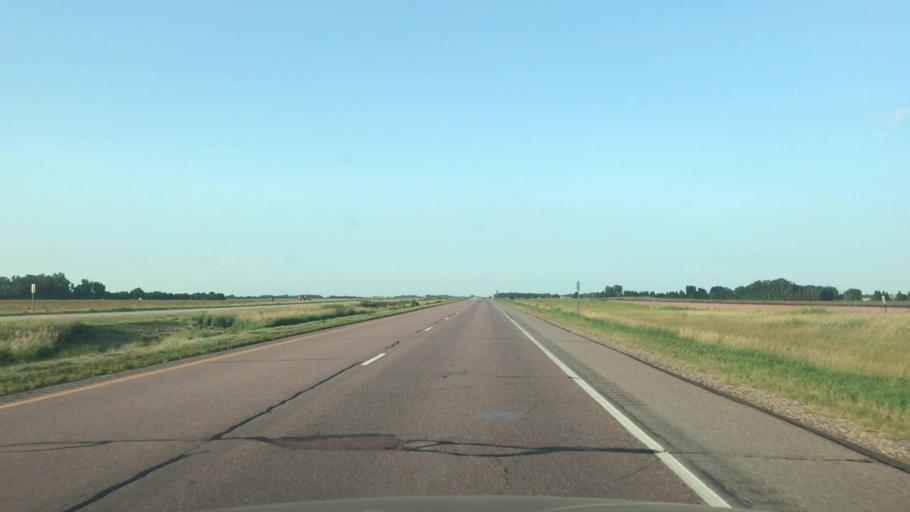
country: US
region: Minnesota
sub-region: Nobles County
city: Worthington
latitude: 43.7404
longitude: -95.4070
